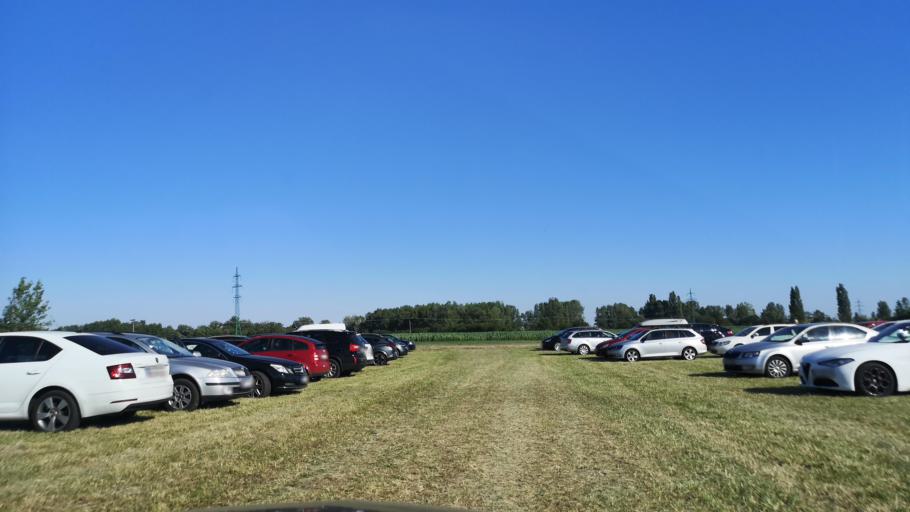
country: SK
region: Trnavsky
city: Dunajska Streda
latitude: 48.0482
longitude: 17.5648
